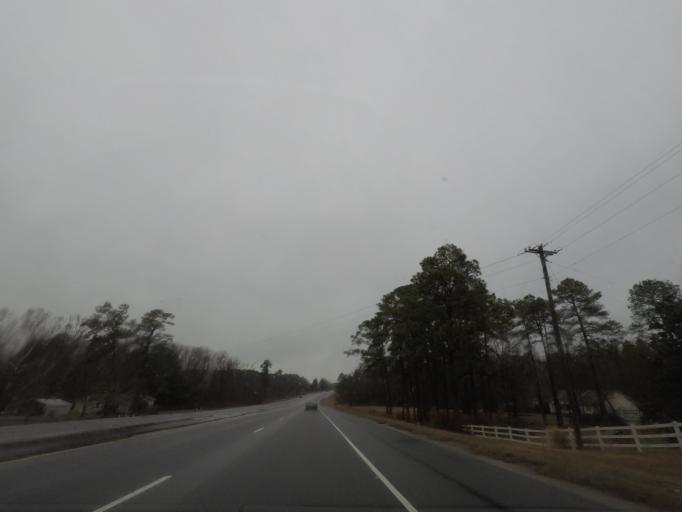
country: US
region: North Carolina
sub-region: Lee County
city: Broadway
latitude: 35.3474
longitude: -79.1072
